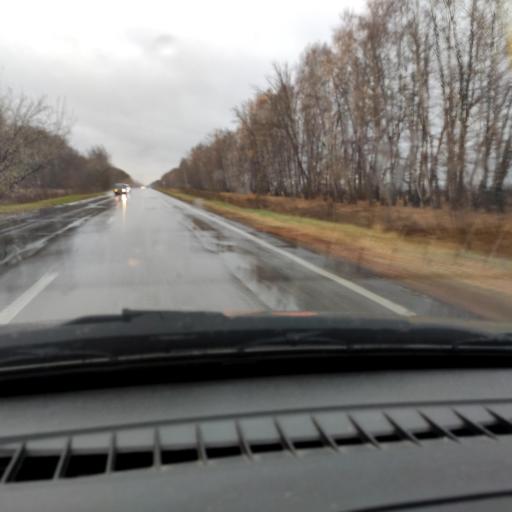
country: RU
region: Samara
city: Khryashchevka
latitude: 53.7243
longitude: 49.2113
